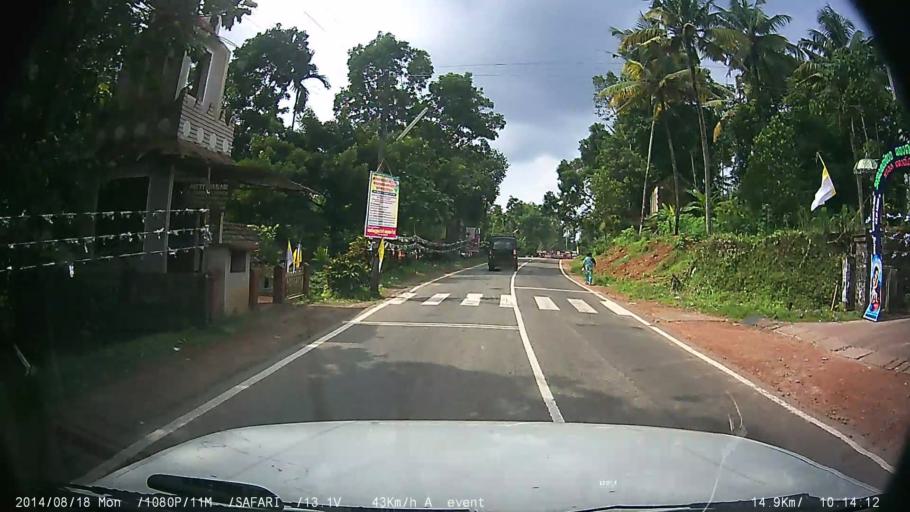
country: IN
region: Kerala
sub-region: Kottayam
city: Palackattumala
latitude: 9.6985
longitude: 76.5580
